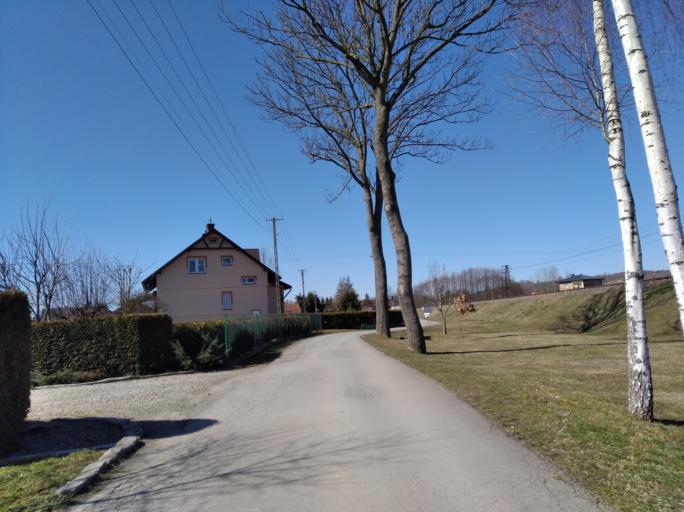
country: PL
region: Subcarpathian Voivodeship
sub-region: Powiat strzyzowski
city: Wysoka Strzyzowska
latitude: 49.8711
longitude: 21.7503
